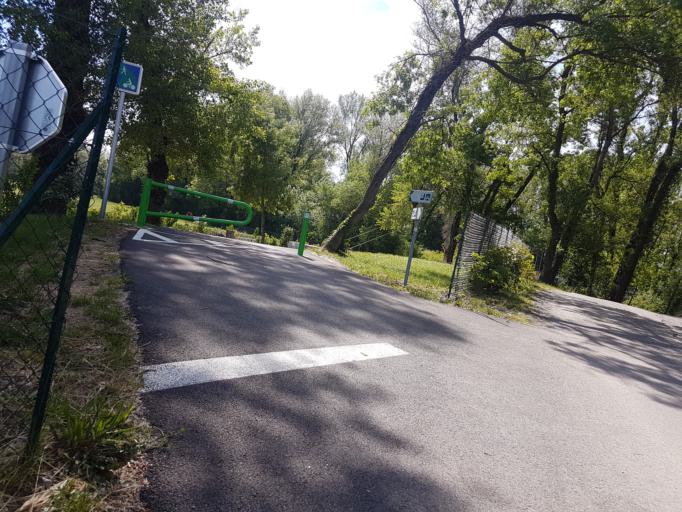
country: FR
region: Rhone-Alpes
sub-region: Departement de l'Ardeche
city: Le Pouzin
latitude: 44.7313
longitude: 4.7569
